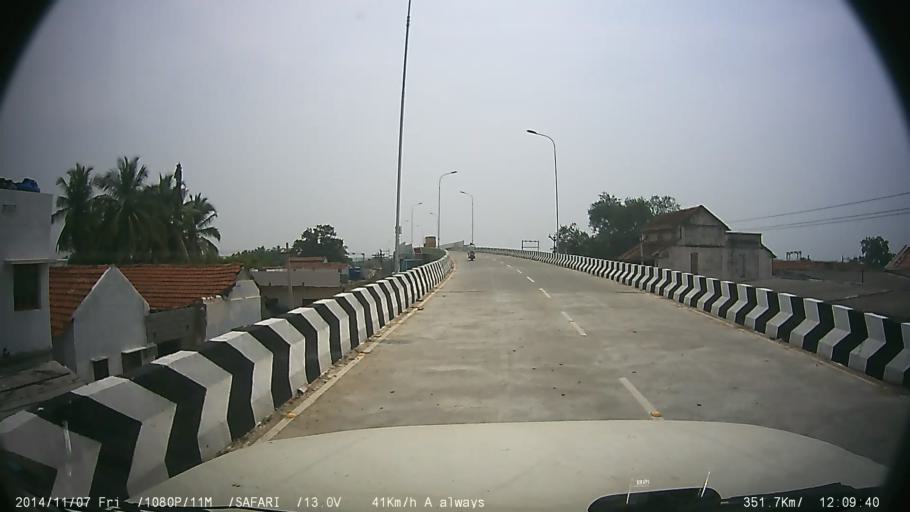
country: IN
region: Tamil Nadu
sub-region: Tiruppur
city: Avinashi
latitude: 11.1195
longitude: 77.2677
